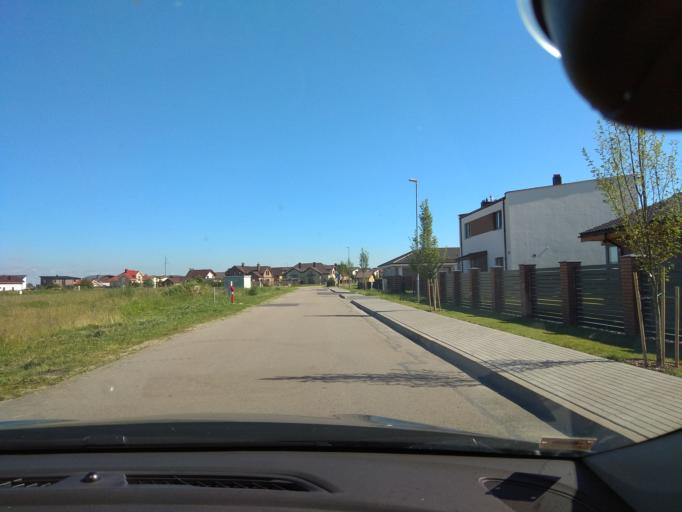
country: LT
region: Klaipedos apskritis
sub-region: Klaipeda
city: Klaipeda
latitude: 55.7504
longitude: 21.1778
